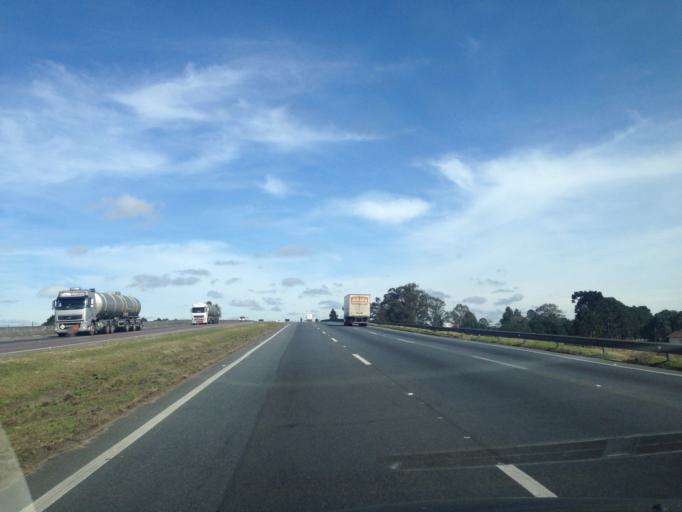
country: BR
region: Parana
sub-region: Sao Jose Dos Pinhais
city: Sao Jose dos Pinhais
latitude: -25.5311
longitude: -49.1444
